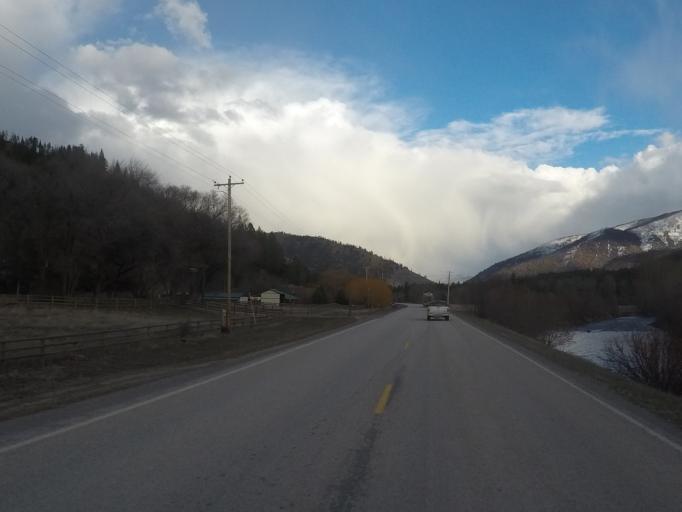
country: US
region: Montana
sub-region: Missoula County
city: Lolo
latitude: 46.7551
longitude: -114.2391
